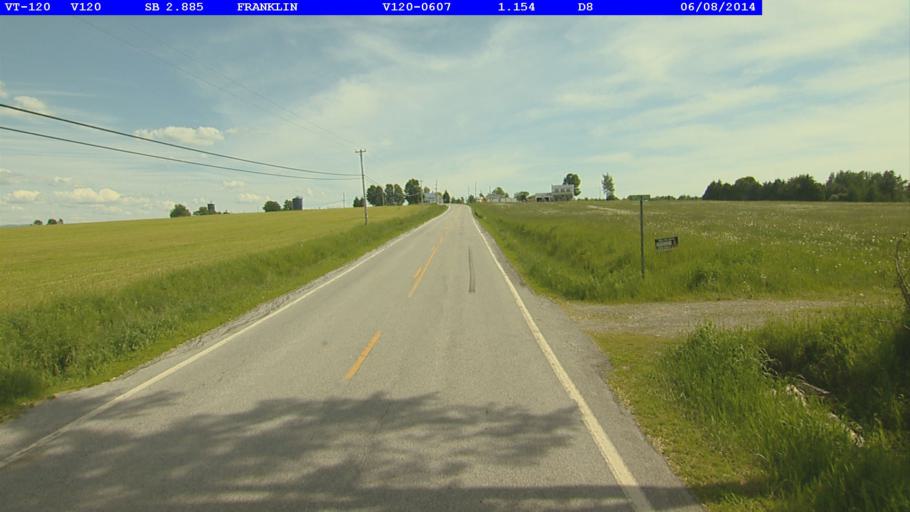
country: US
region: Vermont
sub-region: Franklin County
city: Enosburg Falls
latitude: 44.9496
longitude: -72.9050
